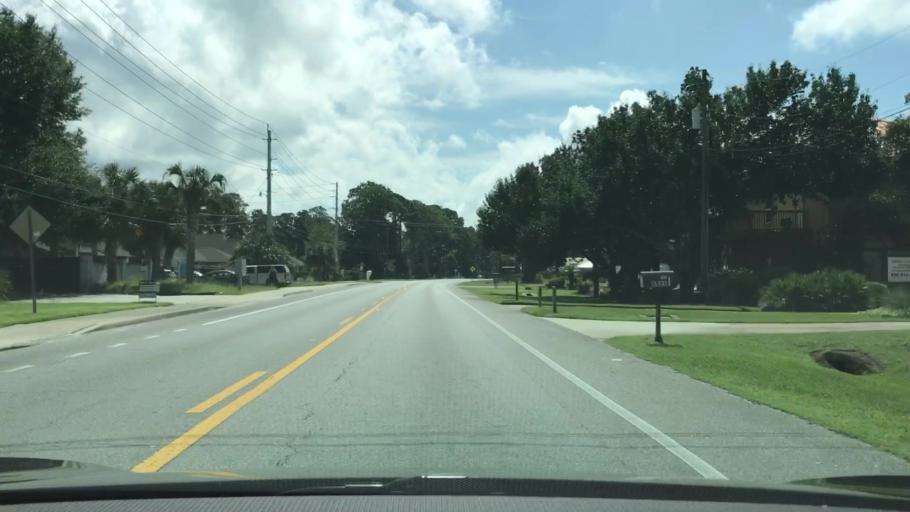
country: US
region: Florida
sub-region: Bay County
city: Lower Grand Lagoon
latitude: 30.1568
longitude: -85.7575
